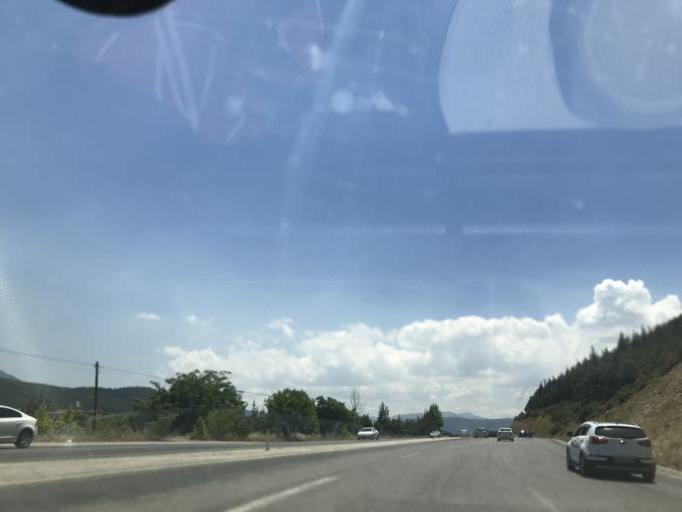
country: TR
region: Denizli
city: Honaz
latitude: 37.7207
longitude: 29.2087
